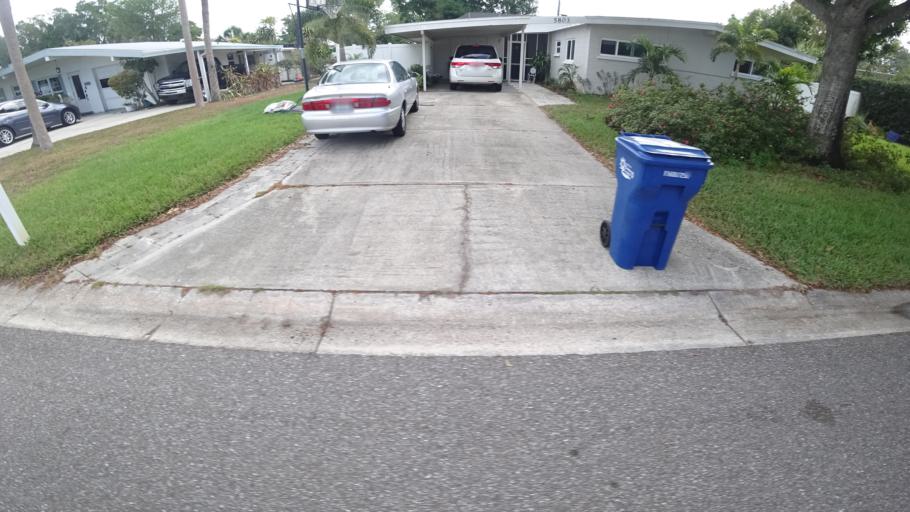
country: US
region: Florida
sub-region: Manatee County
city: Bayshore Gardens
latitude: 27.4386
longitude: -82.5861
